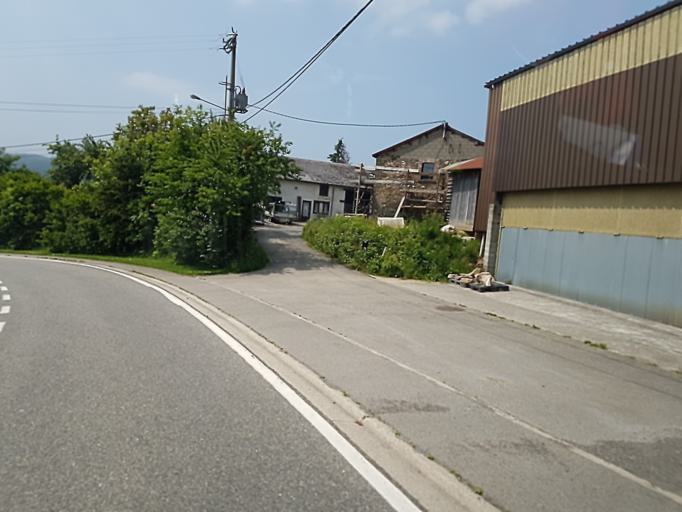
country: BE
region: Wallonia
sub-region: Province de Liege
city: Lierneux
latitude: 50.3299
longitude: 5.7600
